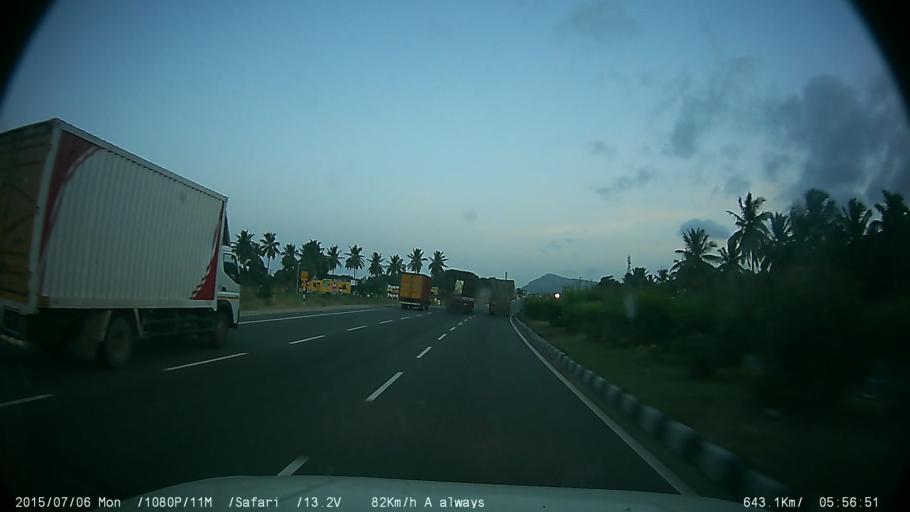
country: IN
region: Tamil Nadu
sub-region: Krishnagiri
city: Krishnagiri
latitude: 12.5773
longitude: 78.1648
